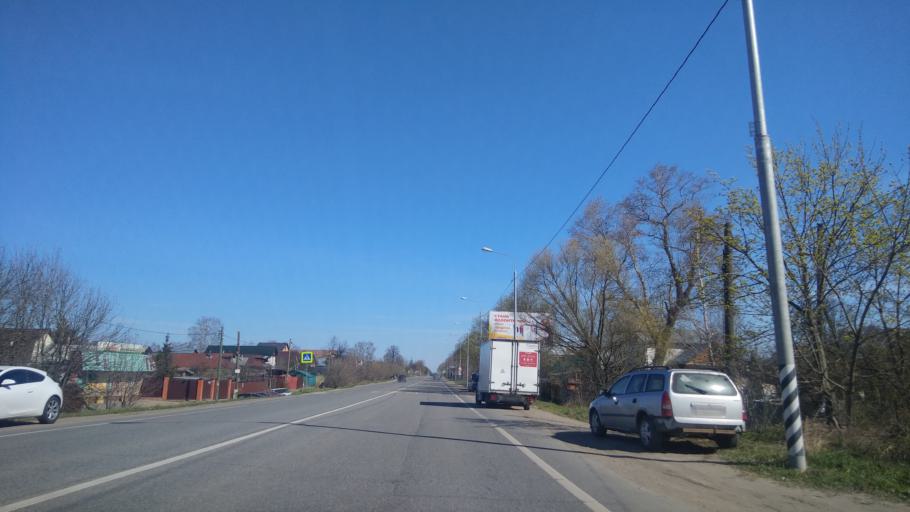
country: RU
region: Moskovskaya
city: Pushkino
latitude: 56.0181
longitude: 37.8717
